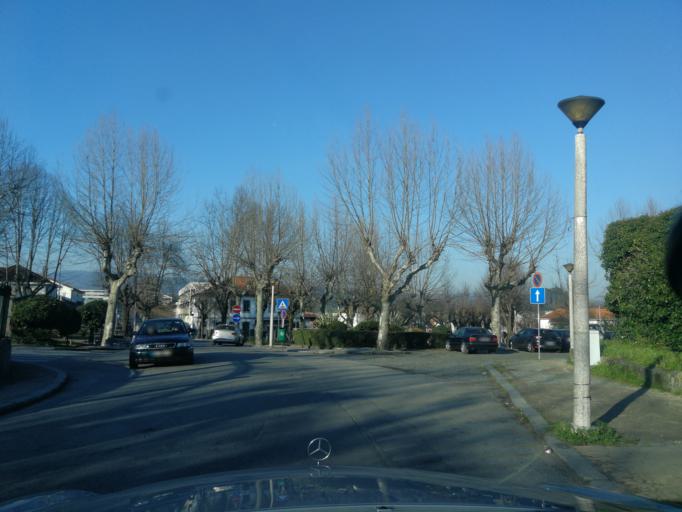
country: PT
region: Braga
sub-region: Guimaraes
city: Ponte
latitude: 41.4854
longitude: -8.3446
